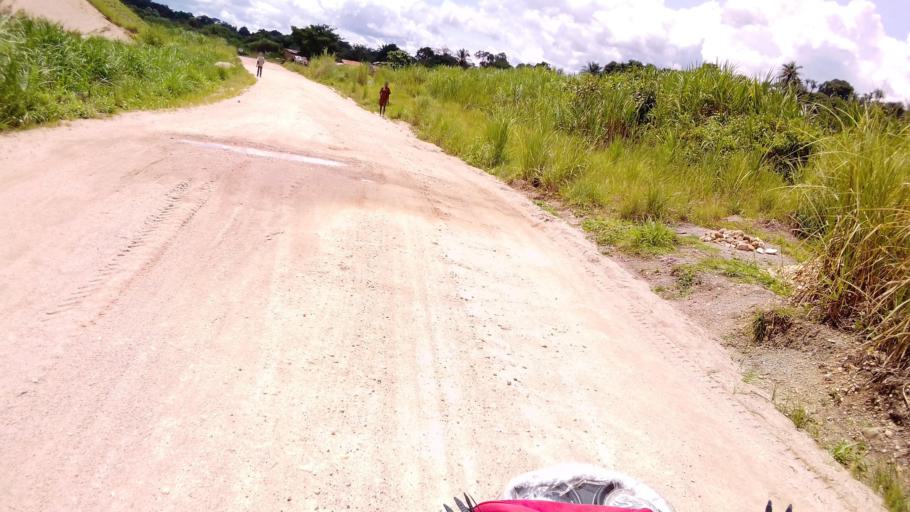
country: SL
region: Eastern Province
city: Koidu
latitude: 8.6738
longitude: -10.9942
